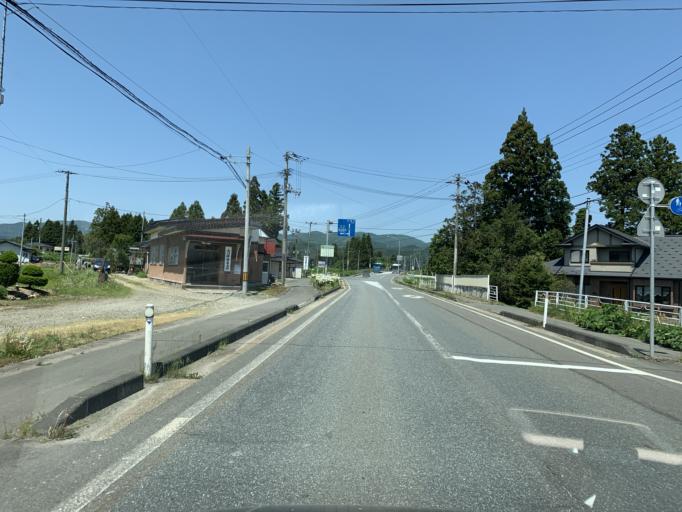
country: JP
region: Iwate
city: Kitakami
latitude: 39.2976
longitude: 140.9803
